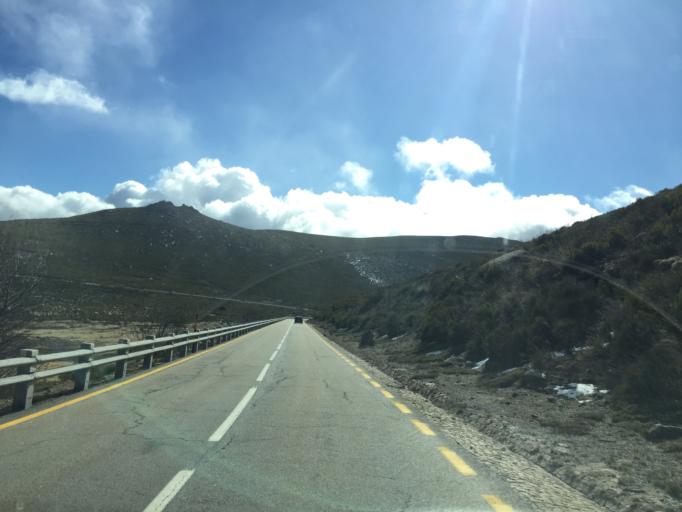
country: PT
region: Castelo Branco
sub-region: Covilha
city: Covilha
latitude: 40.3155
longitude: -7.5863
